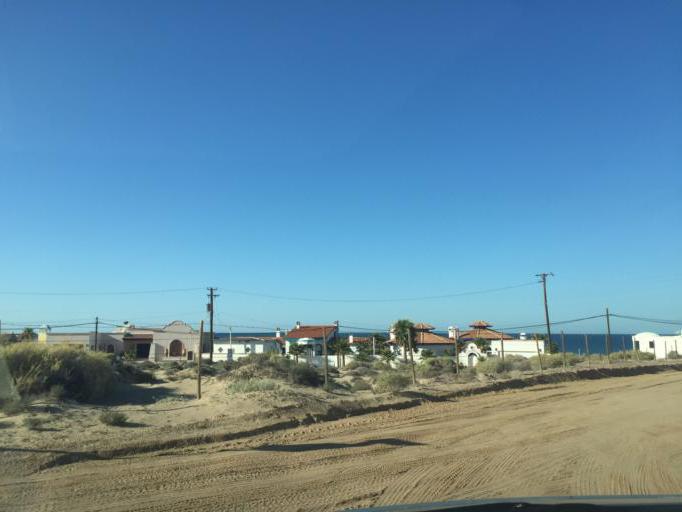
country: MX
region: Sonora
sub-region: Puerto Penasco
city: Puerto Penasco
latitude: 31.2886
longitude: -113.4817
